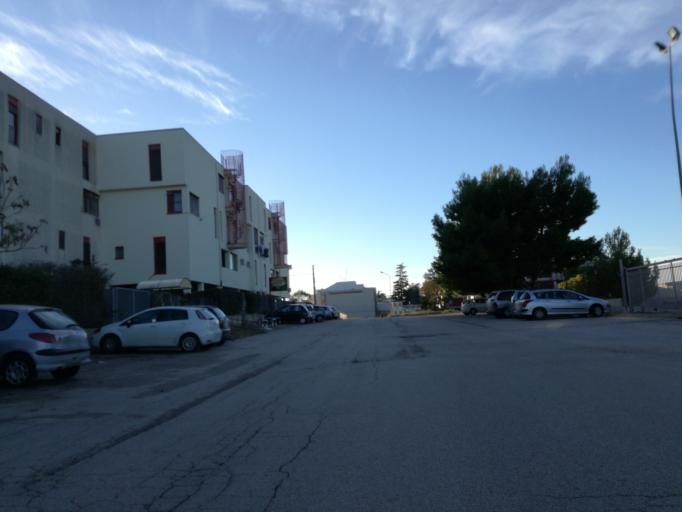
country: IT
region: Apulia
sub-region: Provincia di Bari
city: Adelfia
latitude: 41.0067
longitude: 16.8711
